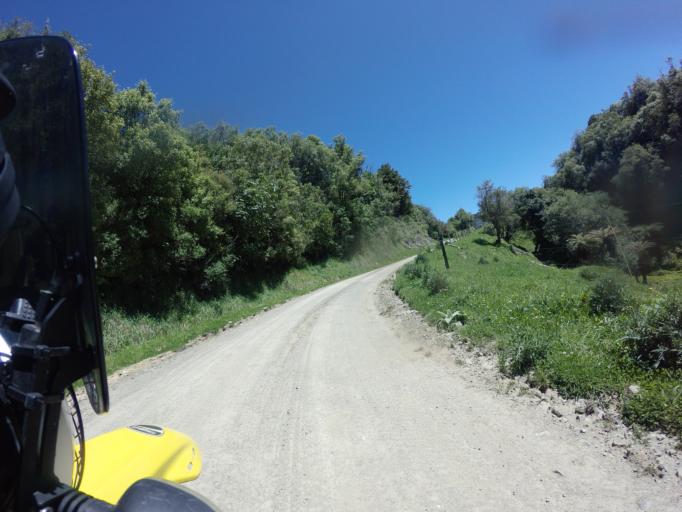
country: NZ
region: Bay of Plenty
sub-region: Opotiki District
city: Opotiki
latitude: -38.4049
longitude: 177.4523
